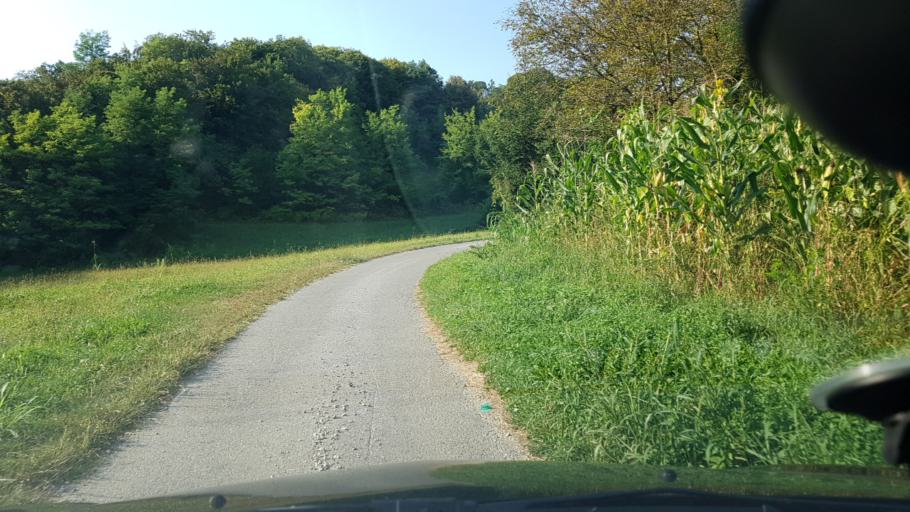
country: HR
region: Krapinsko-Zagorska
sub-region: Grad Krapina
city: Krapina
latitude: 46.1322
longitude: 15.8501
